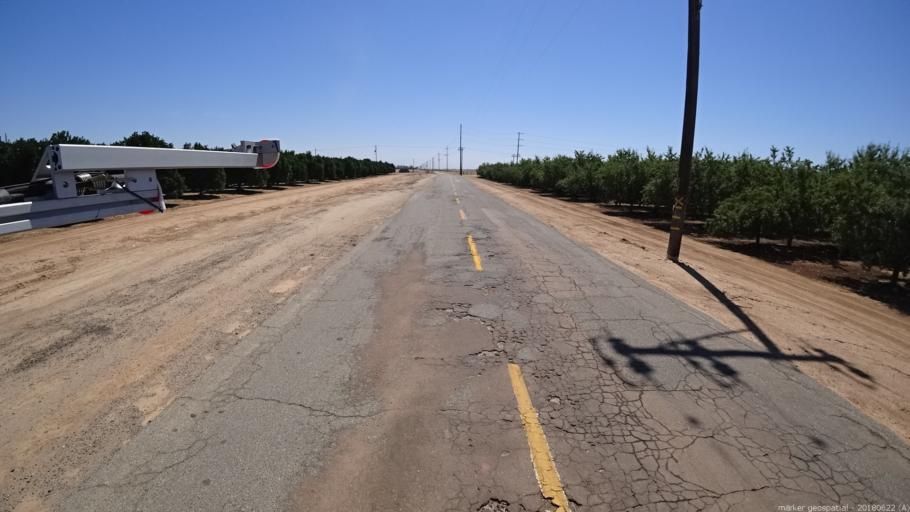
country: US
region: California
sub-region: Madera County
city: Bonadelle Ranchos-Madera Ranchos
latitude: 36.8946
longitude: -119.8229
